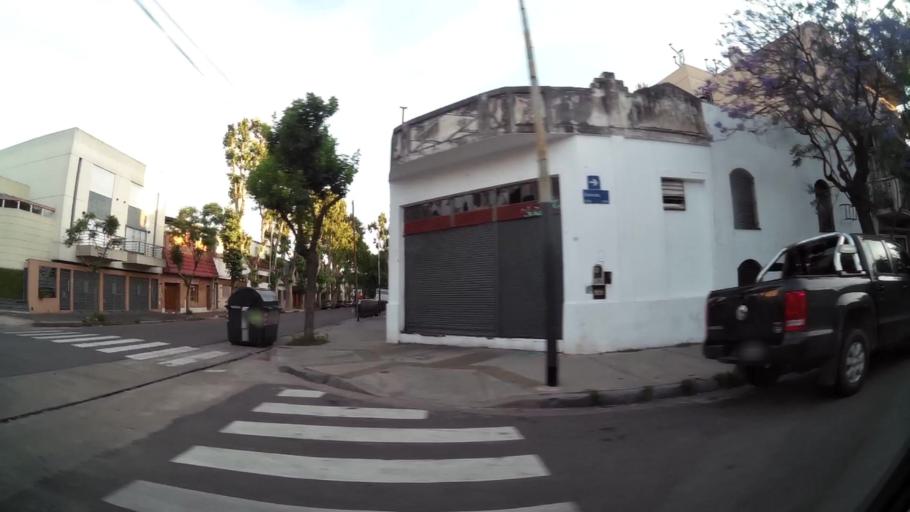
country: AR
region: Buenos Aires F.D.
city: Buenos Aires
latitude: -34.6330
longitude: -58.4117
